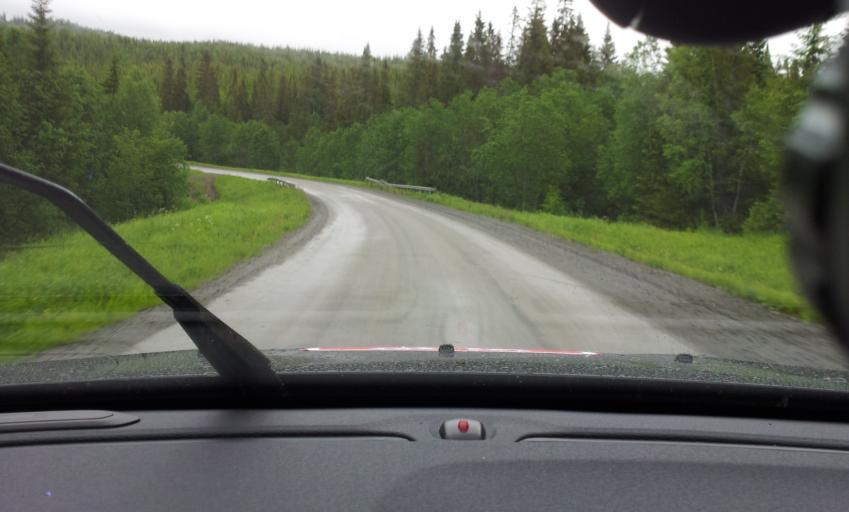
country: SE
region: Jaemtland
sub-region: Are Kommun
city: Are
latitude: 63.4519
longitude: 12.8132
